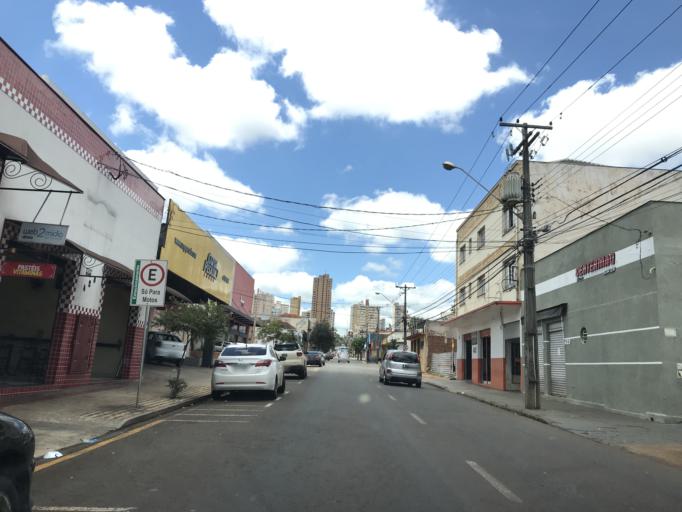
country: BR
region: Parana
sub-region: Londrina
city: Londrina
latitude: -23.3029
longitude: -51.1628
